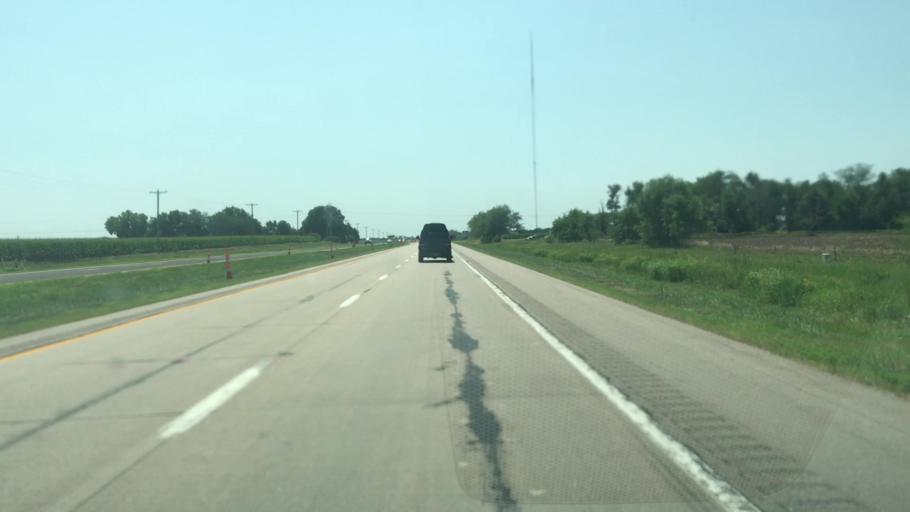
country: US
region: Nebraska
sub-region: Adams County
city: Hastings
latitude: 40.6581
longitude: -98.3824
